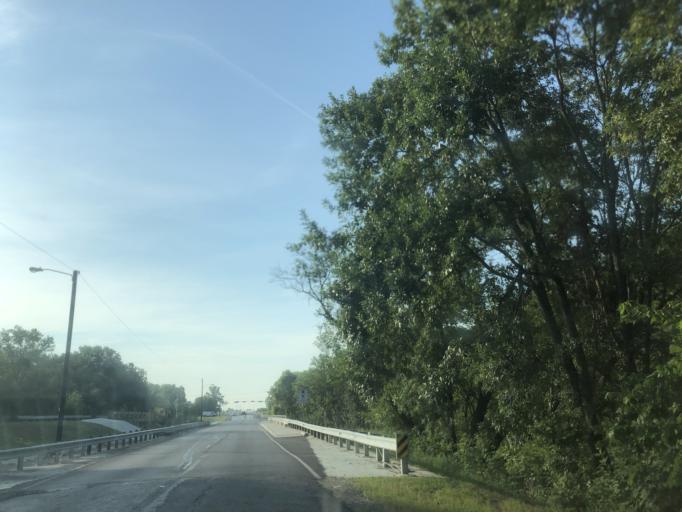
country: US
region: Texas
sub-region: Dallas County
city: Dallas
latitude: 32.7491
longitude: -96.7307
